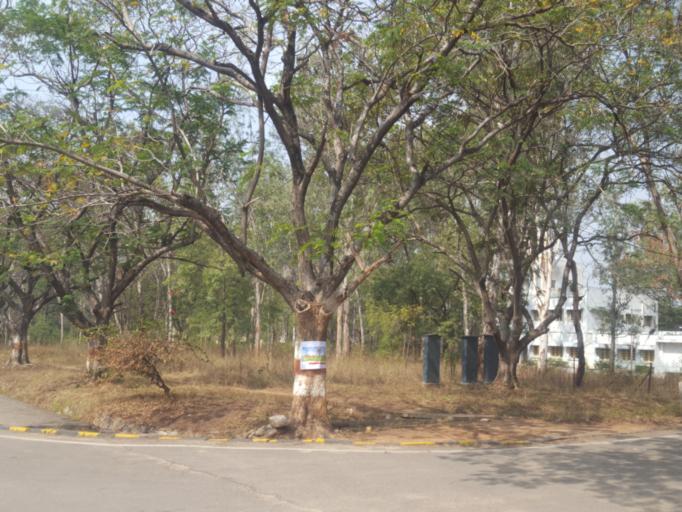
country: IN
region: Telangana
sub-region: Medak
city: Serilingampalle
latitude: 17.4922
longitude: 78.3074
